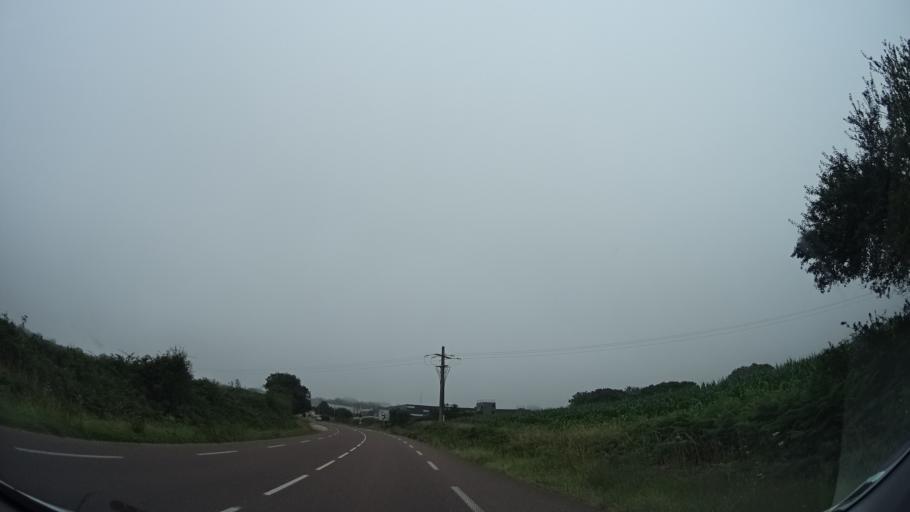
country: FR
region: Lower Normandy
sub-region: Departement de la Manche
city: Les Pieux
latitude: 49.5203
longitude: -1.8143
